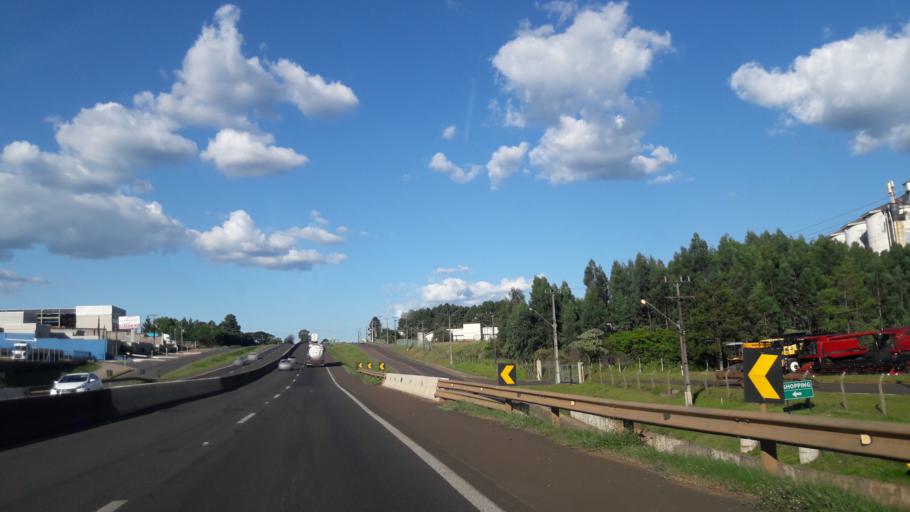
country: BR
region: Parana
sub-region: Guarapuava
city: Guarapuava
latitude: -25.3527
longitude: -51.4590
